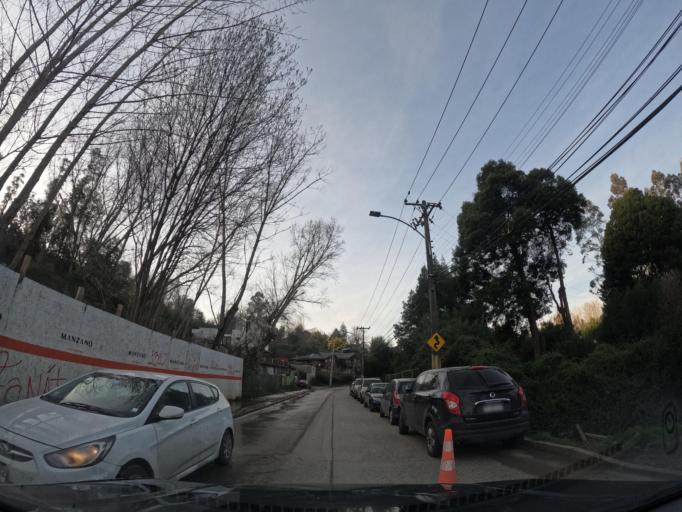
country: CL
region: Biobio
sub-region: Provincia de Concepcion
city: Concepcion
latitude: -36.8416
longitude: -73.0088
